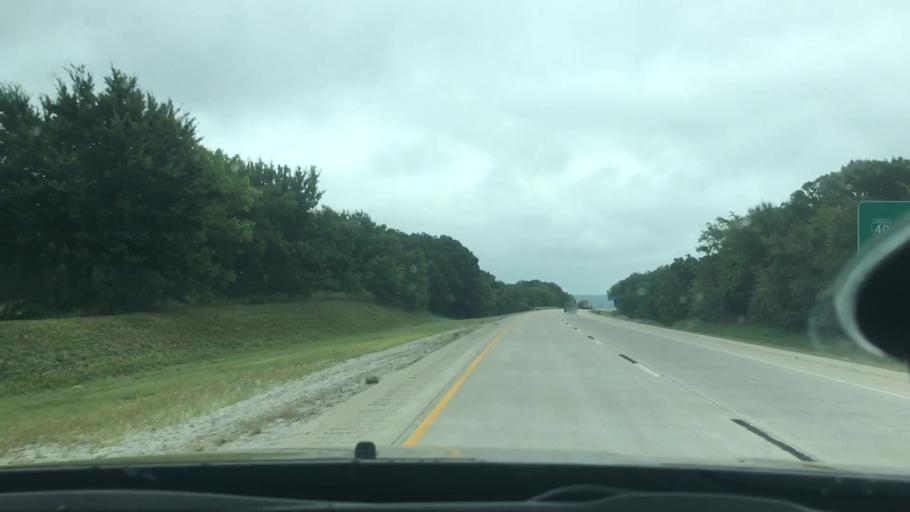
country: US
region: Oklahoma
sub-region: Okmulgee County
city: Henryetta
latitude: 35.4318
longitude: -96.0386
